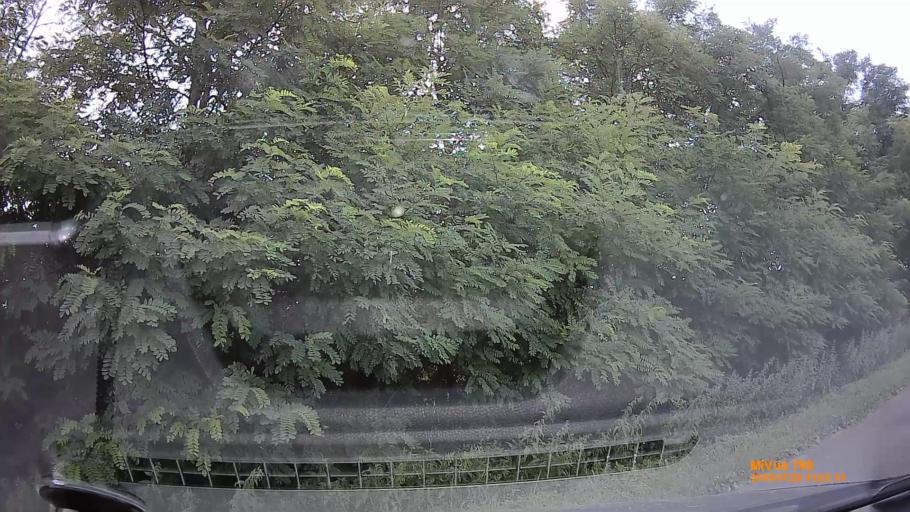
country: HU
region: Szabolcs-Szatmar-Bereg
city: Tarpa
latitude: 48.1594
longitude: 22.5102
